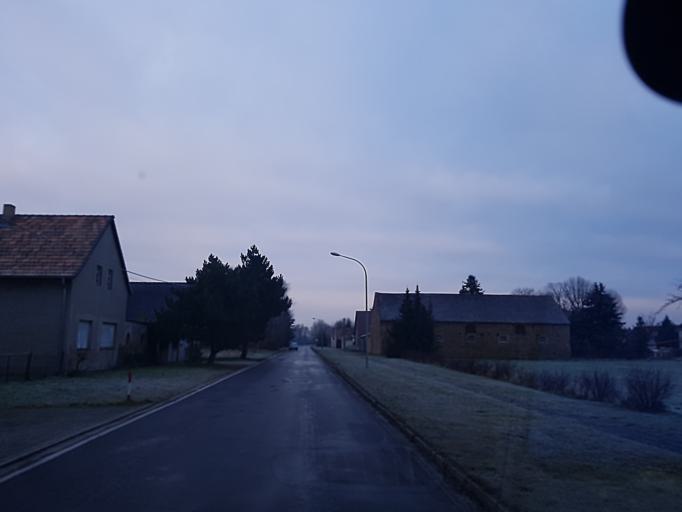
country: DE
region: Brandenburg
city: Finsterwalde
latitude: 51.6620
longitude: 13.7129
